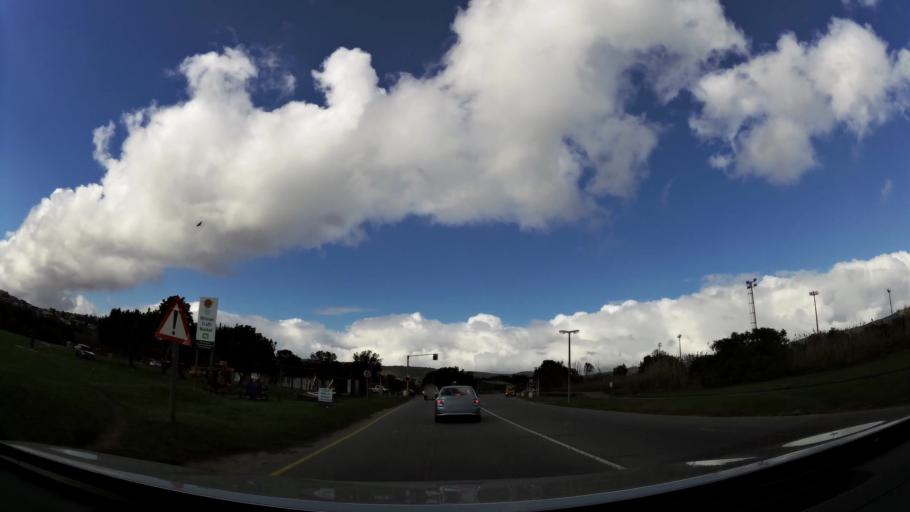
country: ZA
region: Western Cape
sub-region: Eden District Municipality
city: Knysna
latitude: -34.0461
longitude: 23.0697
